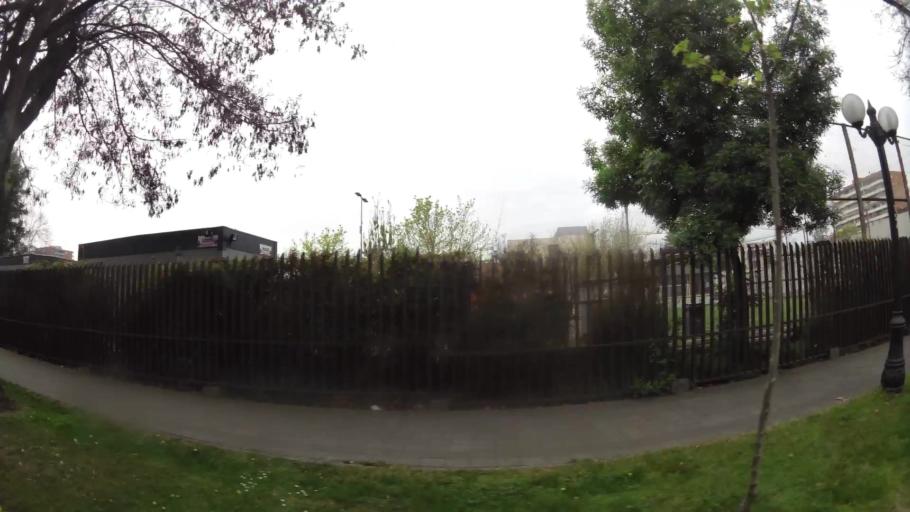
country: CL
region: Santiago Metropolitan
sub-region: Provincia de Santiago
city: Santiago
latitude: -33.4464
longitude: -70.6190
